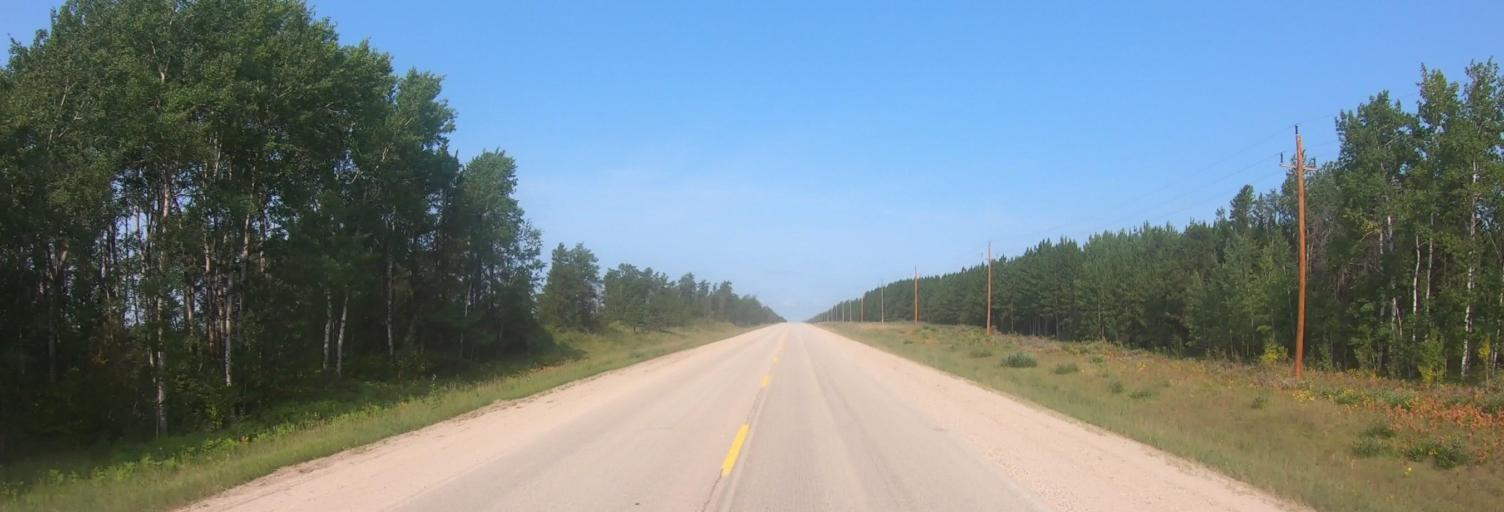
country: US
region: Minnesota
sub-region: Roseau County
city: Roseau
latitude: 49.1202
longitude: -96.0550
